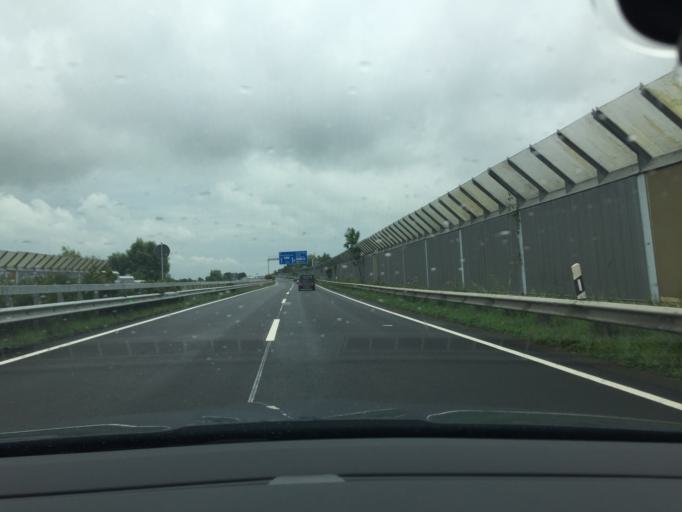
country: DE
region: Lower Saxony
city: Emden
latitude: 53.3870
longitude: 7.1907
